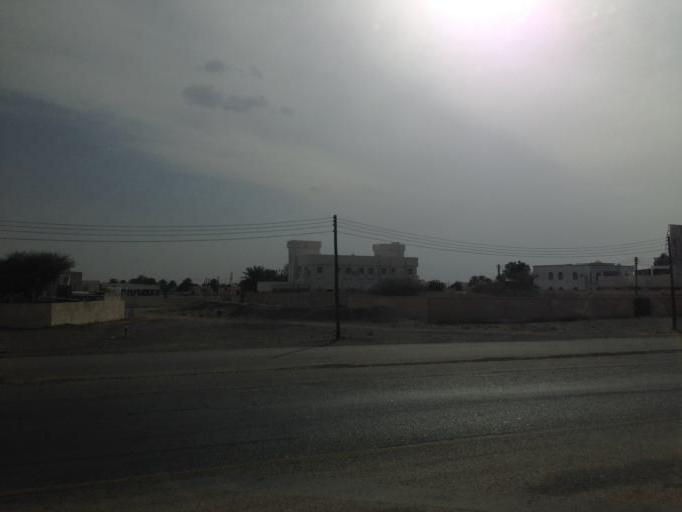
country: OM
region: Ash Sharqiyah
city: Al Qabil
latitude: 22.5745
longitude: 58.6945
